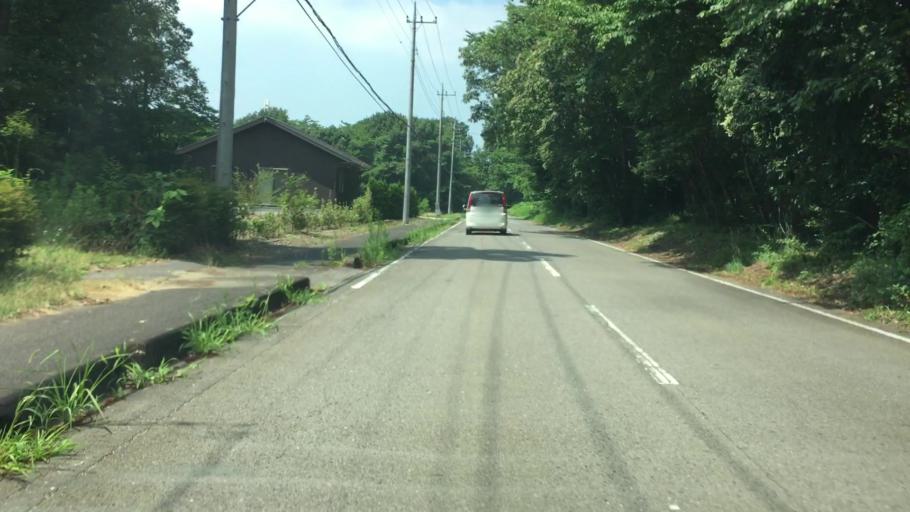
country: JP
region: Tochigi
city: Kuroiso
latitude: 36.9342
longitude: 139.9587
